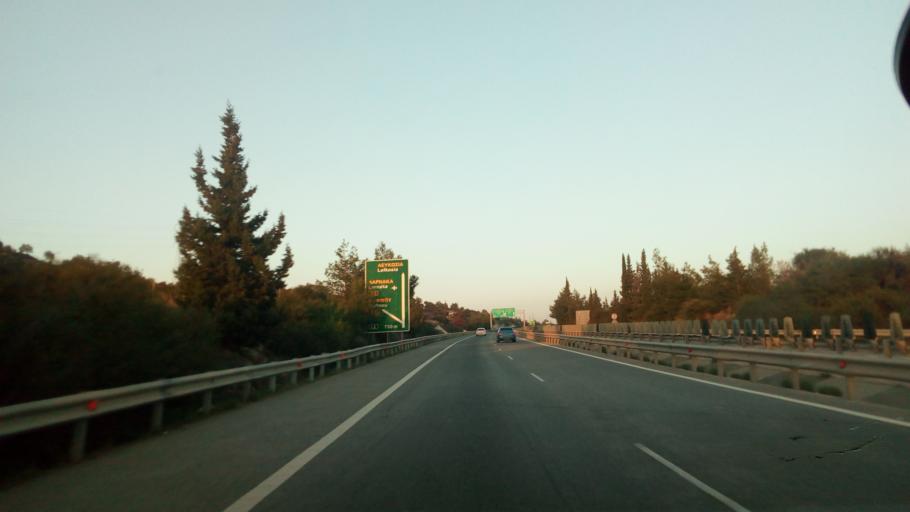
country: CY
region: Larnaka
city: Kofinou
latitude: 34.8291
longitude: 33.3791
